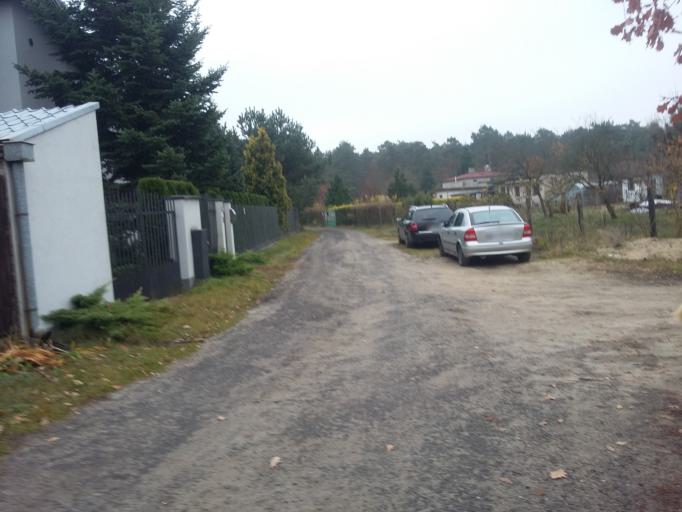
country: PL
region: Lodz Voivodeship
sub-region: Powiat pabianicki
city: Ksawerow
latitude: 51.7298
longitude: 19.3792
